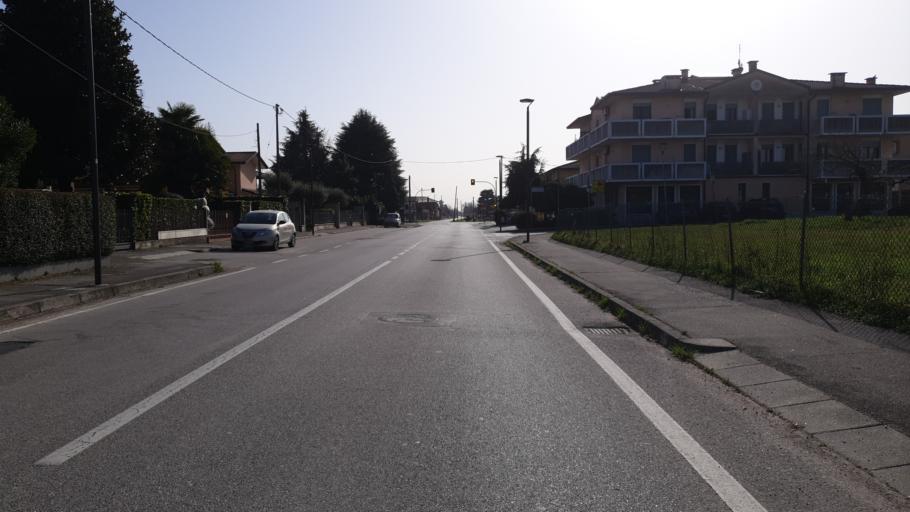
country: IT
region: Veneto
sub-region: Provincia di Padova
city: Cavino
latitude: 45.5153
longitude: 11.8835
